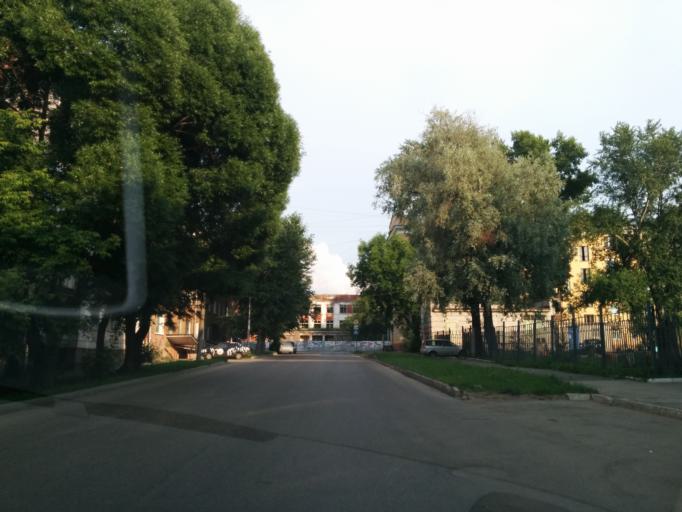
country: RU
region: Perm
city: Perm
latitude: 58.0268
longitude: 56.2956
